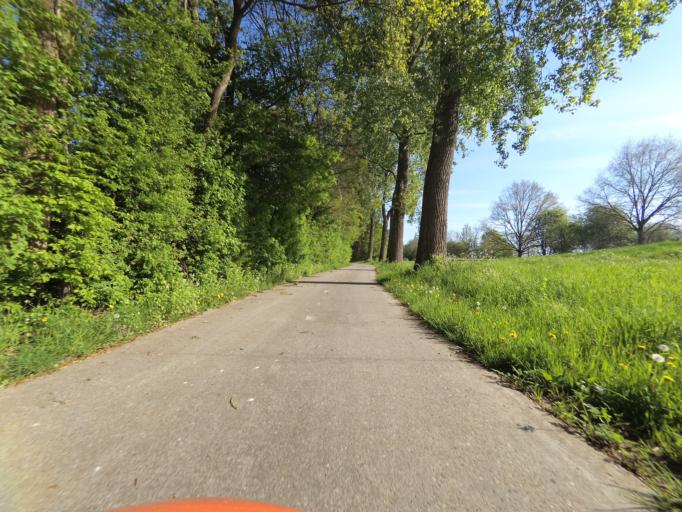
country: NL
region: Gelderland
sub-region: Gemeente Elburg
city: Elburg
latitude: 52.4899
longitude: 5.8438
